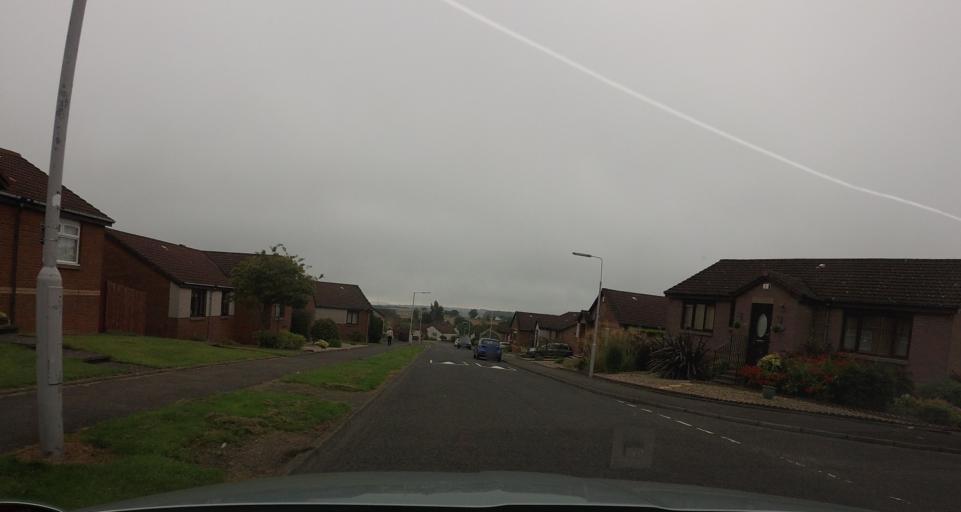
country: GB
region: Scotland
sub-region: Fife
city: Kelty
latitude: 56.1354
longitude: -3.3756
